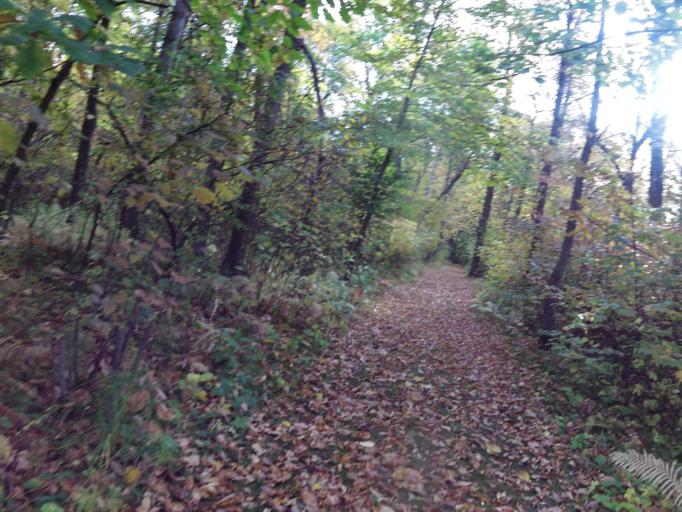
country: US
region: North Dakota
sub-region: Pembina County
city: Cavalier
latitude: 48.7786
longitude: -97.7347
